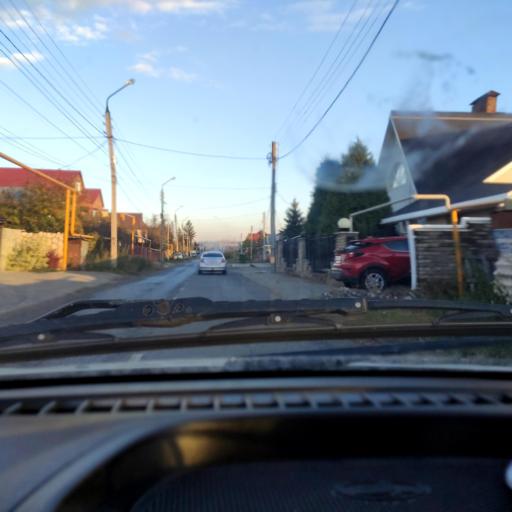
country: RU
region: Samara
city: Zhigulevsk
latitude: 53.4647
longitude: 49.6232
